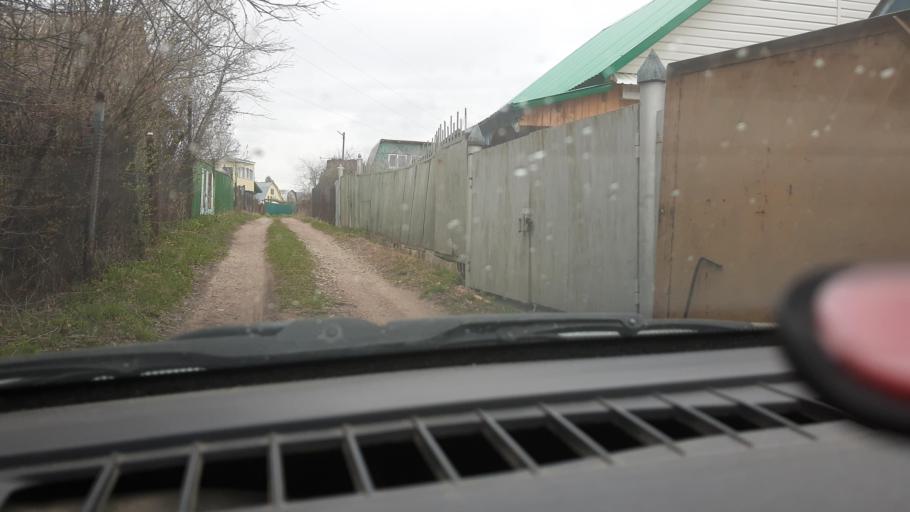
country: RU
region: Bashkortostan
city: Mikhaylovka
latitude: 54.9206
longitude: 55.8878
